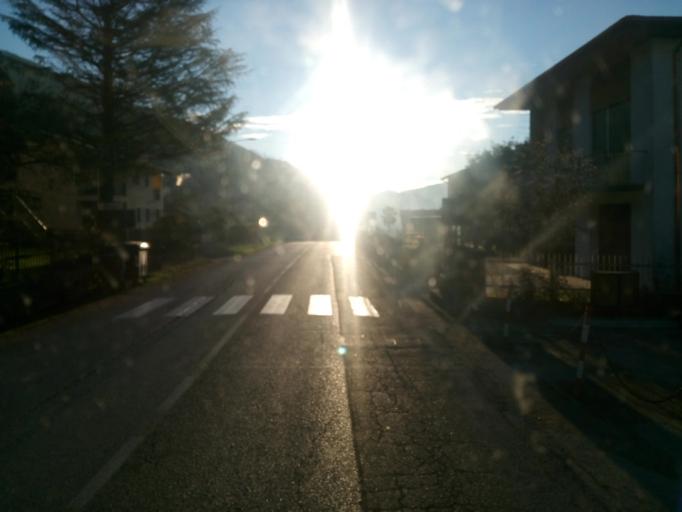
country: IT
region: Veneto
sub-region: Provincia di Vicenza
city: Valli del Pasubio
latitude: 45.7375
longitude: 11.2664
